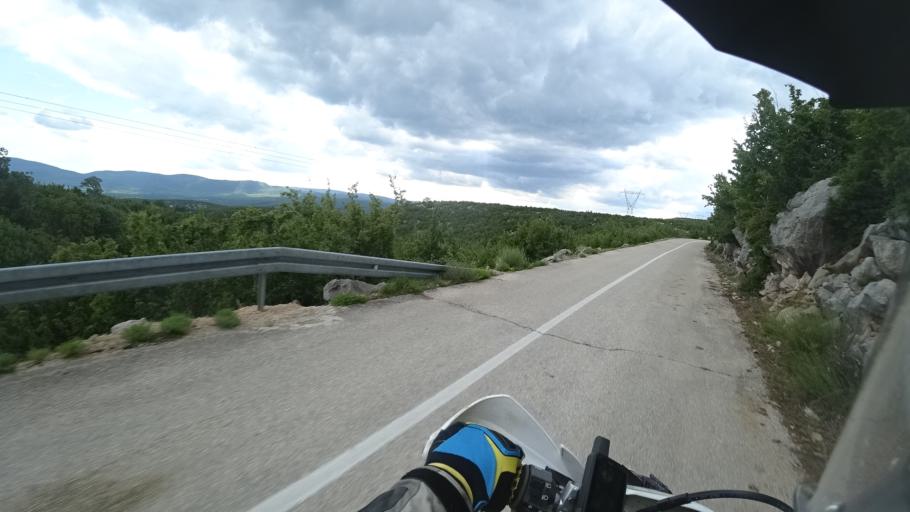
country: HR
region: Zadarska
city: Gracac
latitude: 44.1997
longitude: 15.8684
